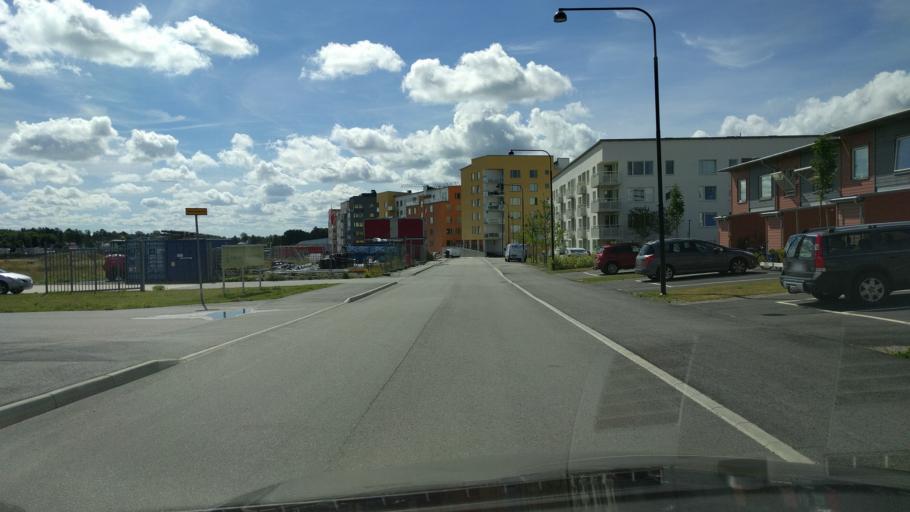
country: SE
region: Stockholm
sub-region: Jarfalla Kommun
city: Jakobsberg
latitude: 59.4170
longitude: 17.8682
